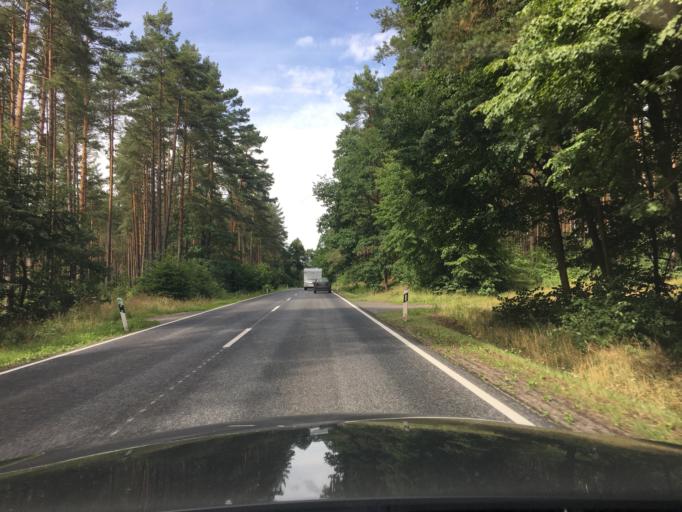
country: DE
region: Brandenburg
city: Furstenberg
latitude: 53.2353
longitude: 13.1144
